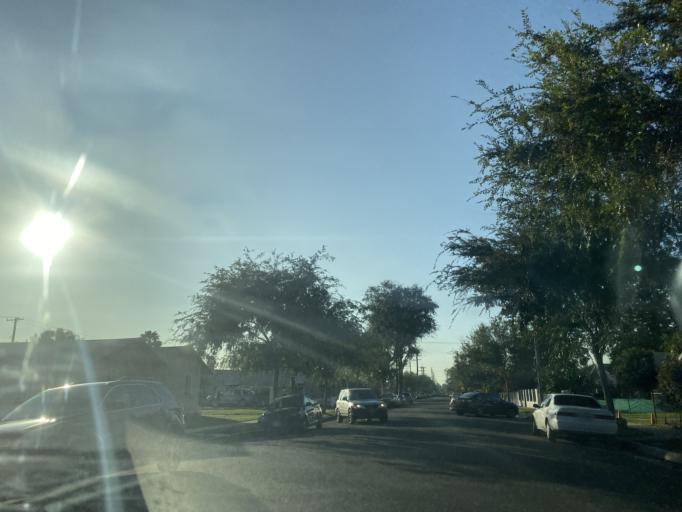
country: US
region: California
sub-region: Orange County
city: Fullerton
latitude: 33.8674
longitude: -117.9164
